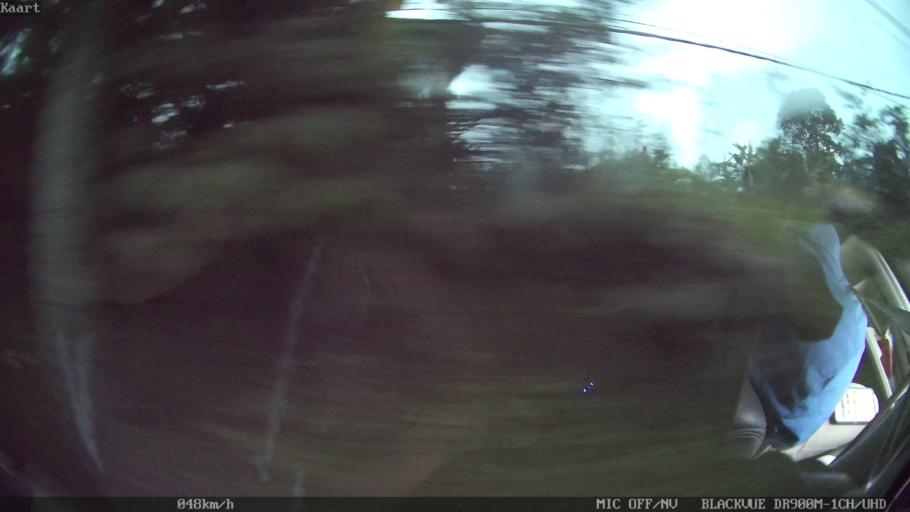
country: ID
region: Bali
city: Banjar Taro Kelod
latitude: -8.3127
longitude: 115.3024
